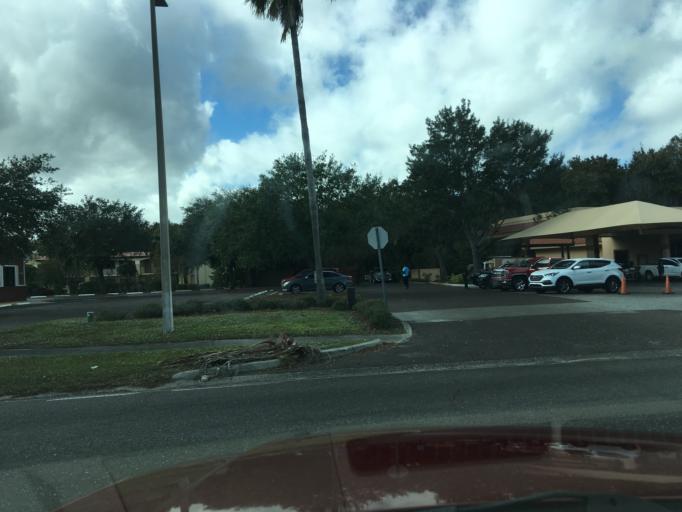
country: US
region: Florida
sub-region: Hillsborough County
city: Sun City Center
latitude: 27.7143
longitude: -82.3770
